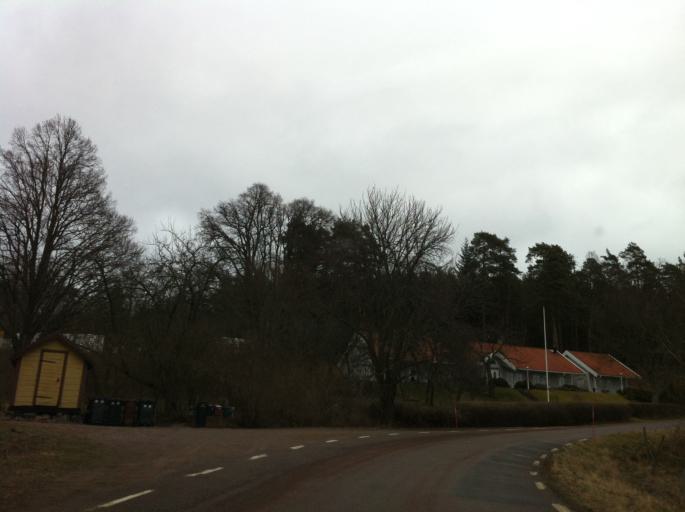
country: SE
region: Kalmar
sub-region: Vasterviks Kommun
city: Vaestervik
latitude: 57.9091
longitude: 16.6548
